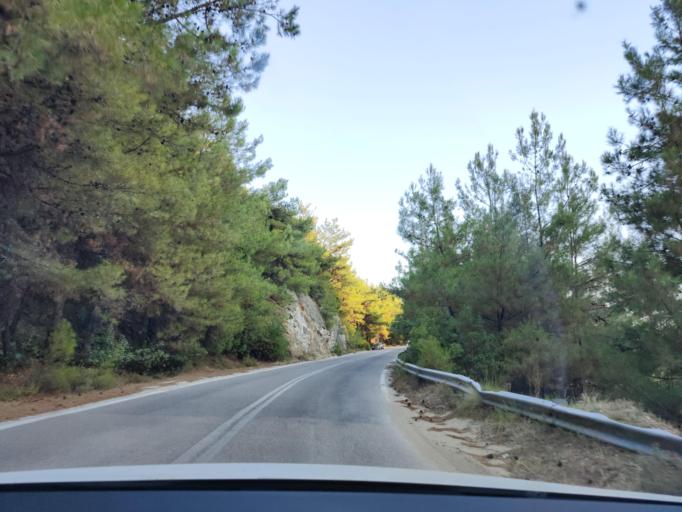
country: GR
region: East Macedonia and Thrace
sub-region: Nomos Kavalas
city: Potamia
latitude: 40.6282
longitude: 24.7655
